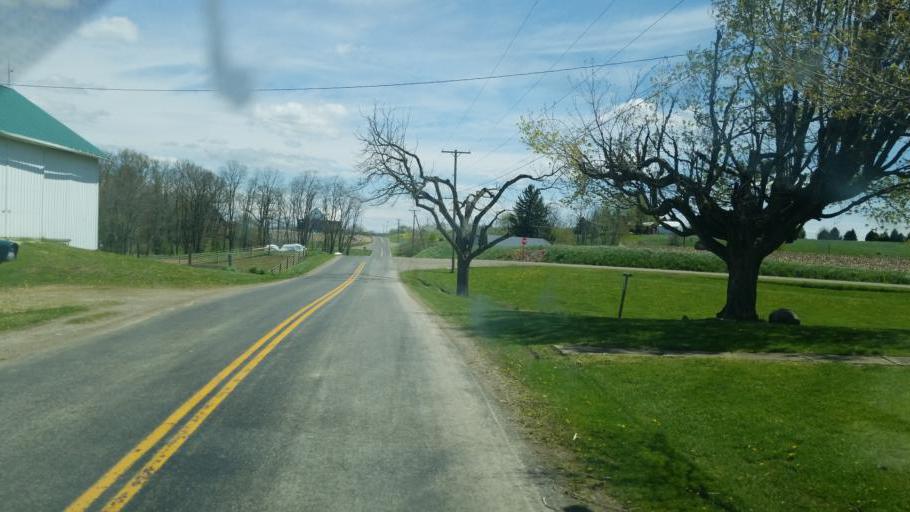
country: US
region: Ohio
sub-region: Ashland County
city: Loudonville
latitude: 40.7561
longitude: -82.1492
